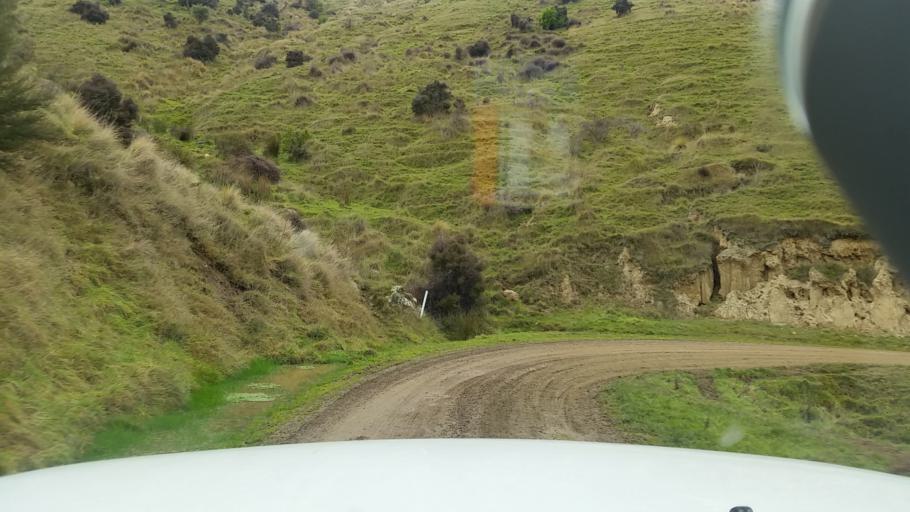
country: NZ
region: Canterbury
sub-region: Christchurch City
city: Christchurch
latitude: -43.6421
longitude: 172.8385
